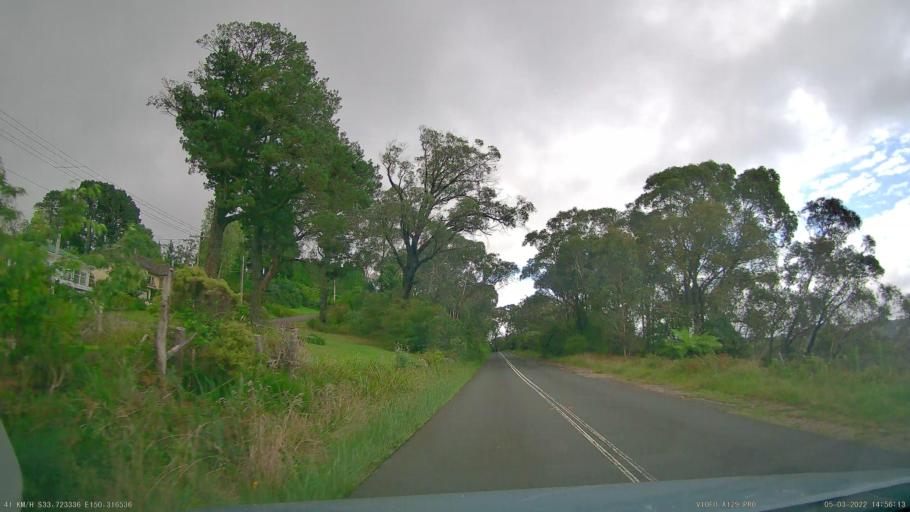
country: AU
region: New South Wales
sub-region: Blue Mountains Municipality
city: Katoomba
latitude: -33.7231
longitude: 150.3166
